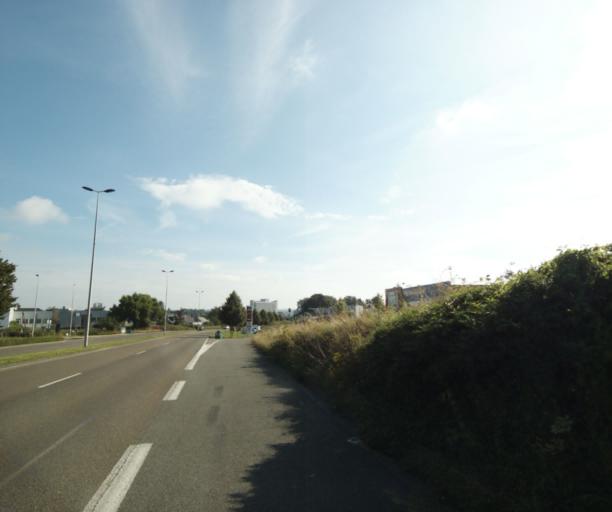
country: FR
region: Pays de la Loire
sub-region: Departement de la Mayenne
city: Laval
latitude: 48.0562
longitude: -0.7909
